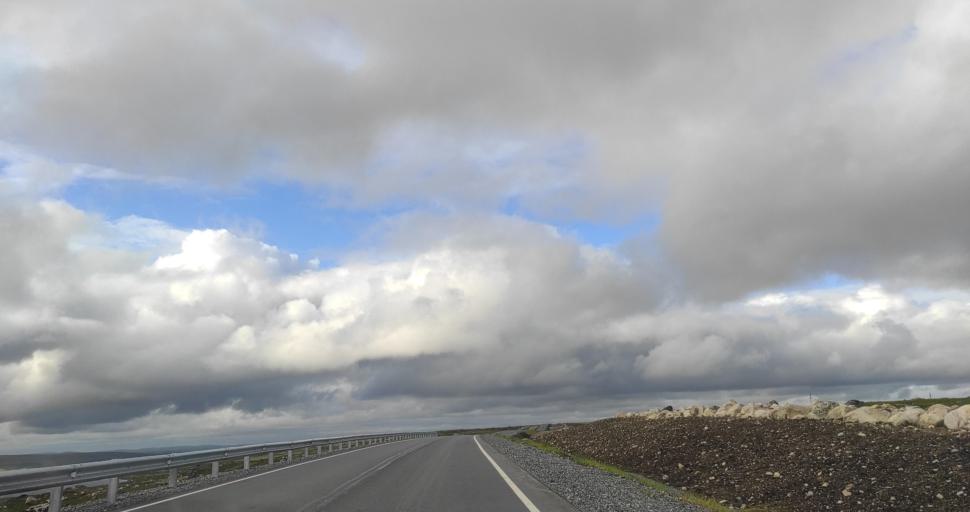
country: RU
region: Murmansk
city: Teriberka
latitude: 68.8807
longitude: 34.9049
